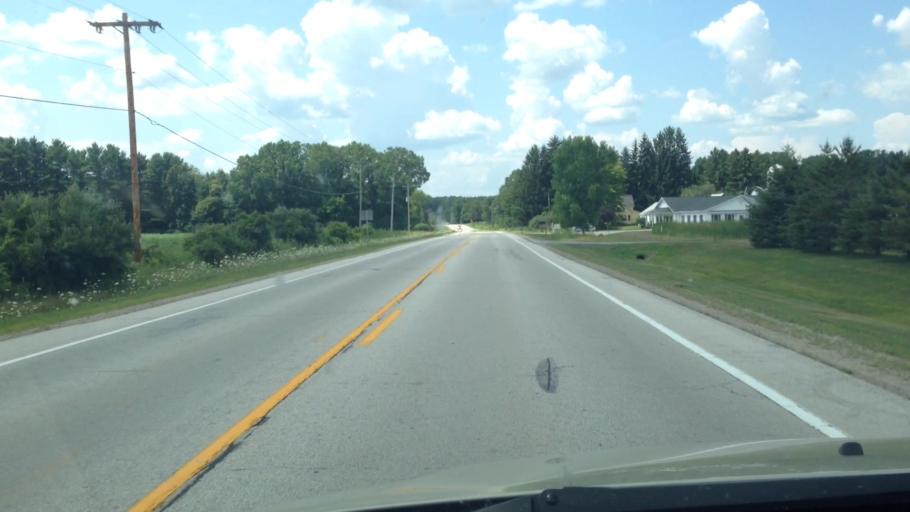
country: US
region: Wisconsin
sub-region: Brown County
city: Suamico
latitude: 44.6445
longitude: -88.0913
